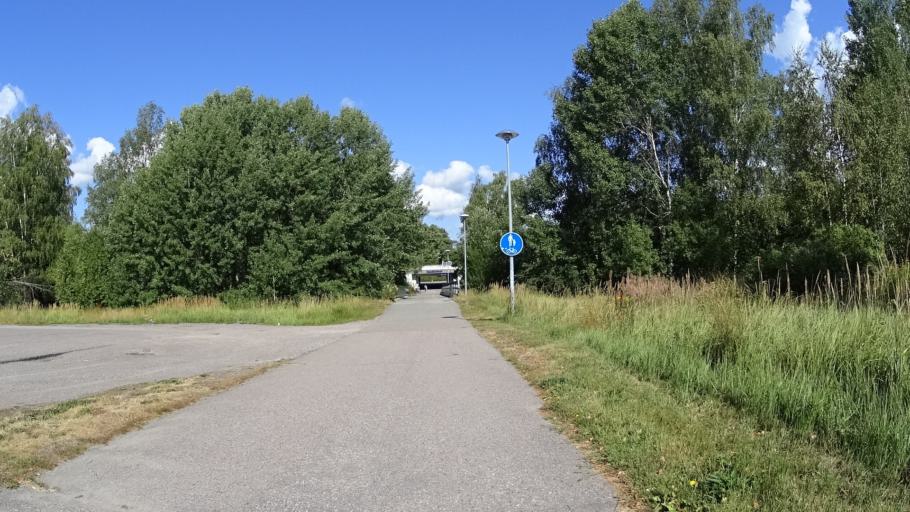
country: FI
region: Uusimaa
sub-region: Helsinki
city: Espoo
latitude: 60.1878
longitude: 24.6011
